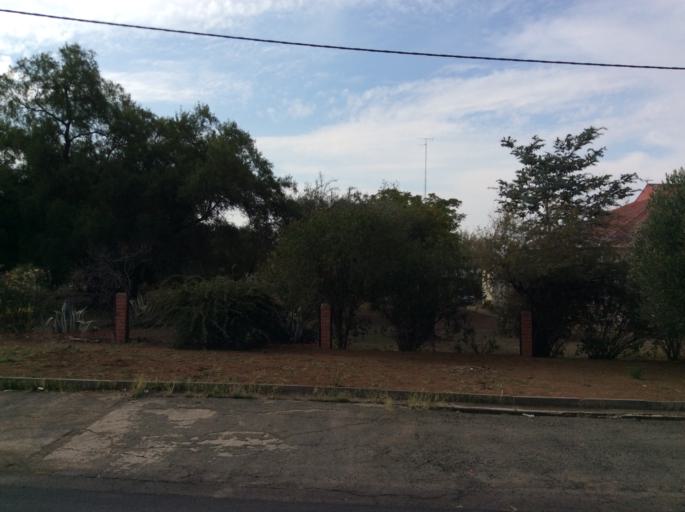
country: ZA
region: Orange Free State
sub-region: Xhariep District Municipality
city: Dewetsdorp
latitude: -29.5793
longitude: 26.6624
